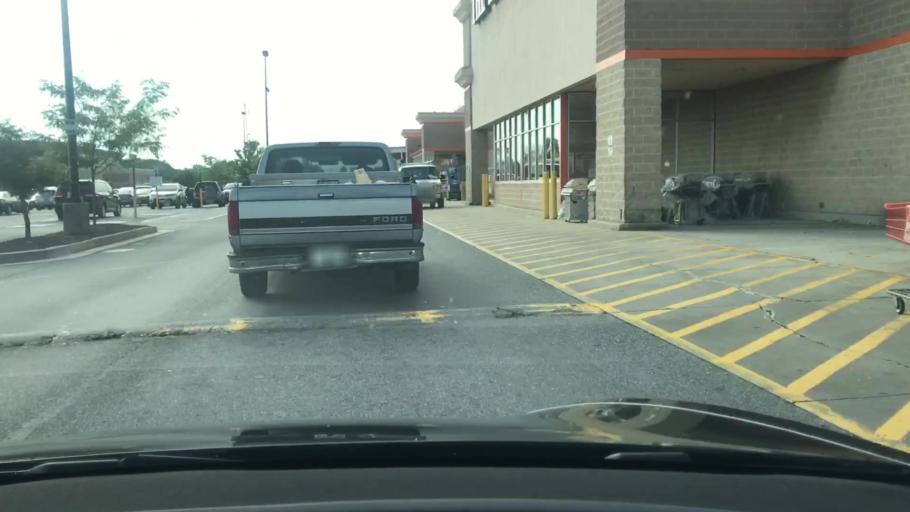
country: US
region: Maryland
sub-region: Baltimore County
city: Rossville
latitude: 39.3356
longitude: -76.4893
